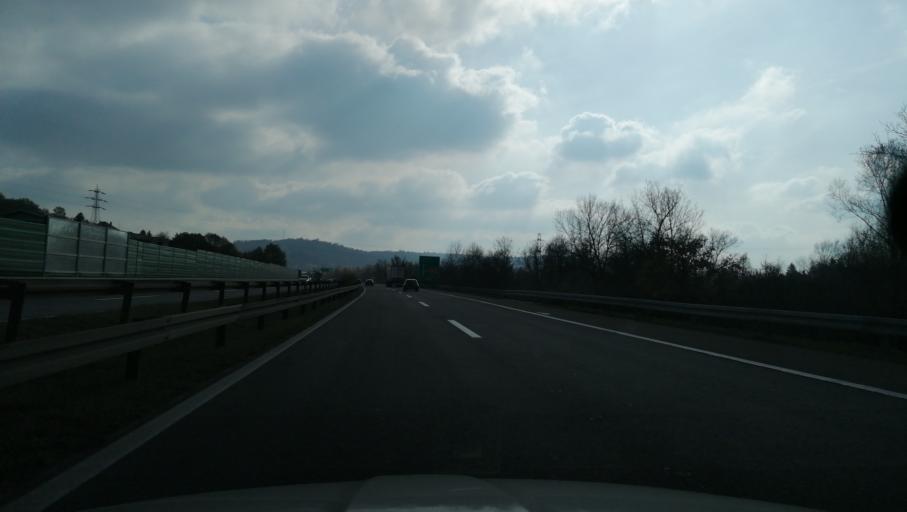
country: RS
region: Central Serbia
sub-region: Belgrade
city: Zvezdara
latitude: 44.6803
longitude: 20.5860
